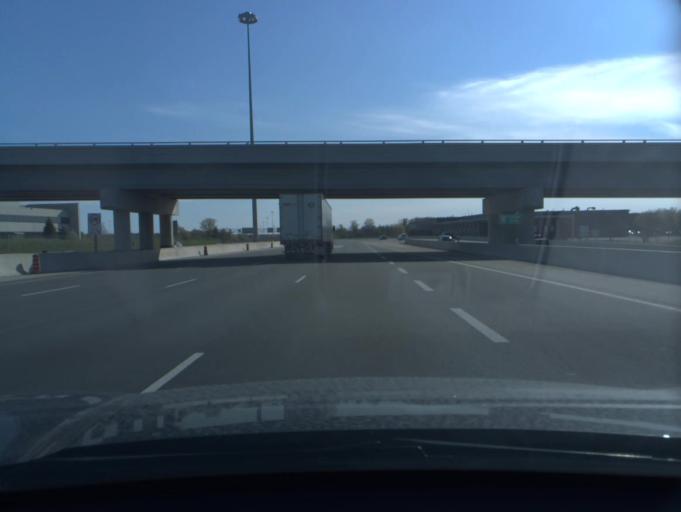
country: CA
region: Ontario
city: North Perth
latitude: 43.8100
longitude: -80.9998
